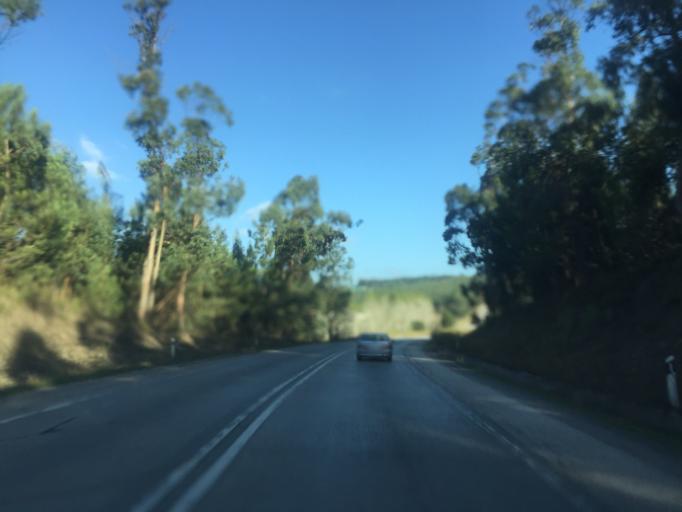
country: PT
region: Santarem
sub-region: Rio Maior
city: Rio Maior
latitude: 39.2931
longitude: -8.9475
